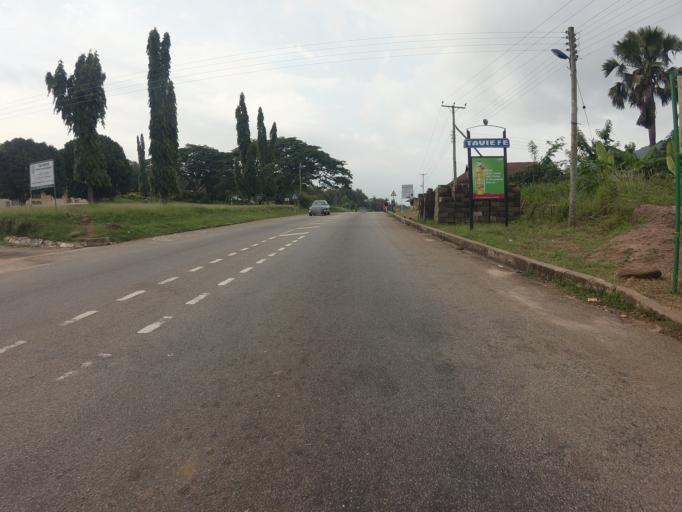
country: GH
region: Volta
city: Ho
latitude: 6.6605
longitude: 0.4718
